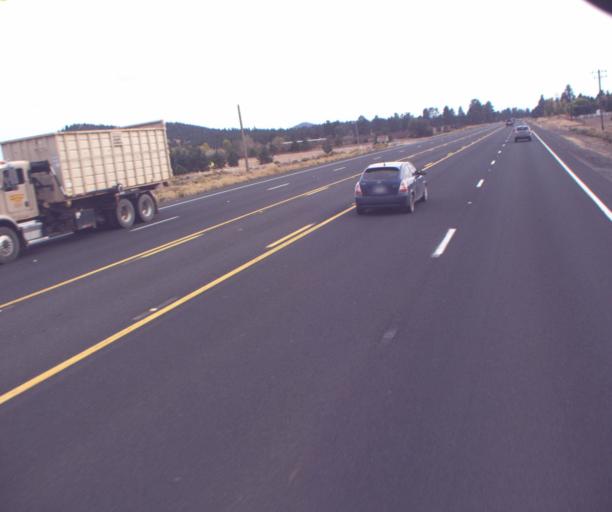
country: US
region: Arizona
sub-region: Coconino County
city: Flagstaff
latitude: 35.2947
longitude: -111.5426
